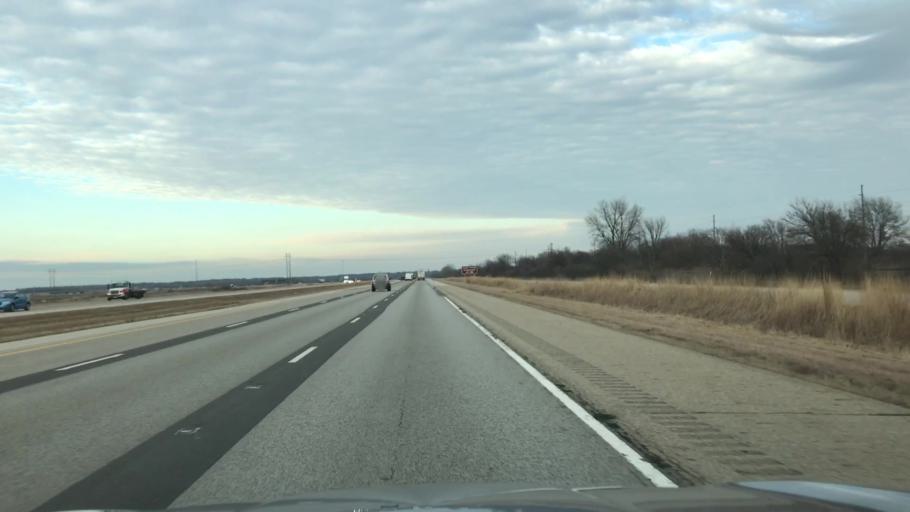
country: US
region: Illinois
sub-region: Logan County
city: Lincoln
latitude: 40.0946
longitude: -89.4215
